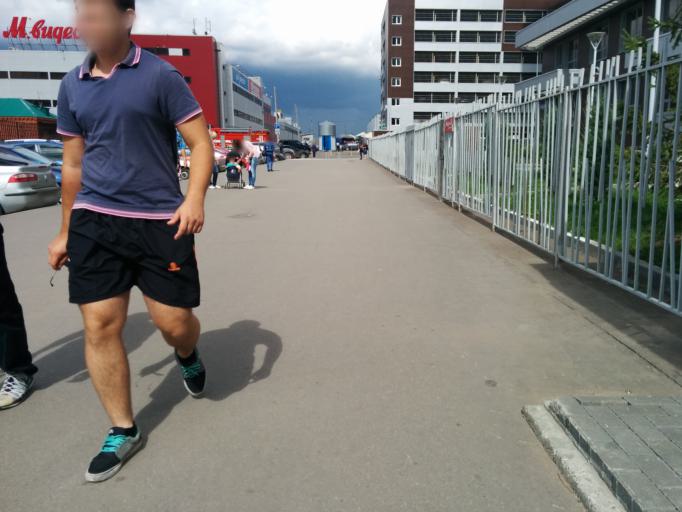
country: RU
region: Tatarstan
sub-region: Gorod Kazan'
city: Kazan
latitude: 55.7472
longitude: 49.2055
